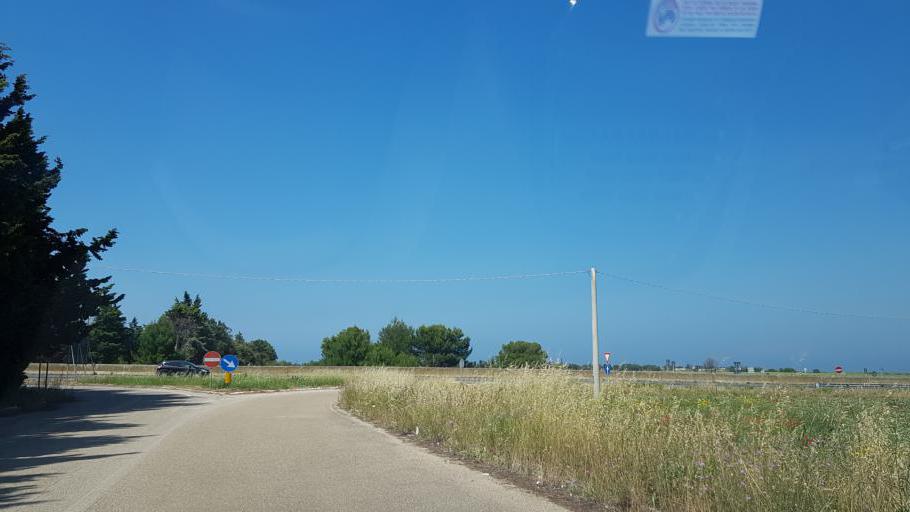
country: IT
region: Apulia
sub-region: Provincia di Brindisi
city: Brindisi
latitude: 40.6689
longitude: 17.8605
